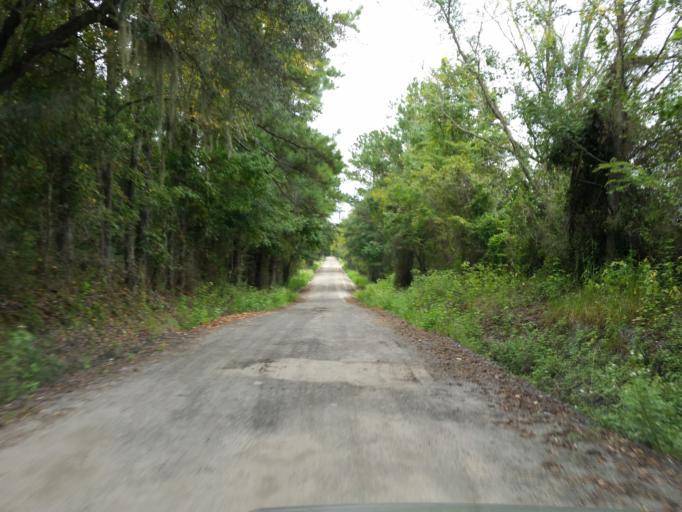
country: US
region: Florida
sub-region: Alachua County
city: High Springs
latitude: 29.9575
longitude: -82.5594
